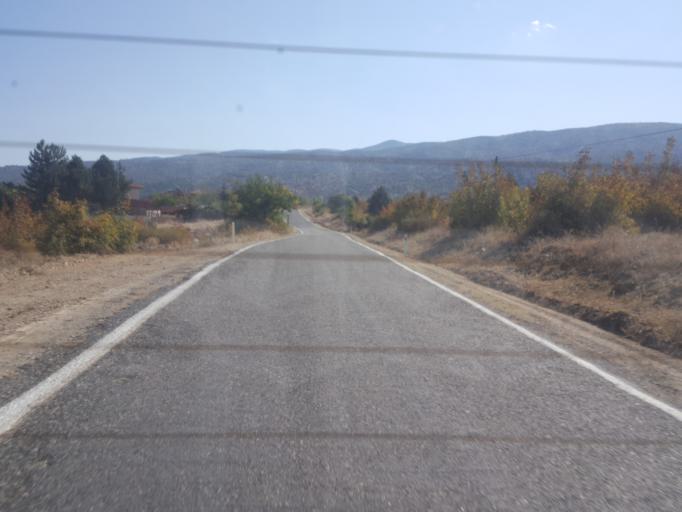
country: TR
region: Kastamonu
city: Tosya
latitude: 41.0015
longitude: 34.1543
